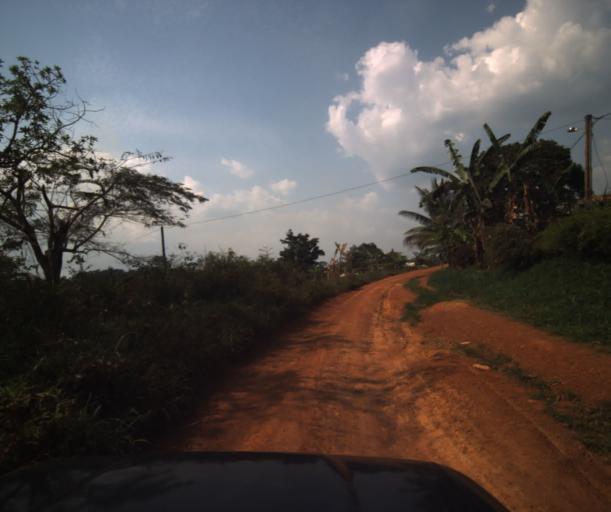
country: CM
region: Centre
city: Akono
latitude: 3.5960
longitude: 11.3032
